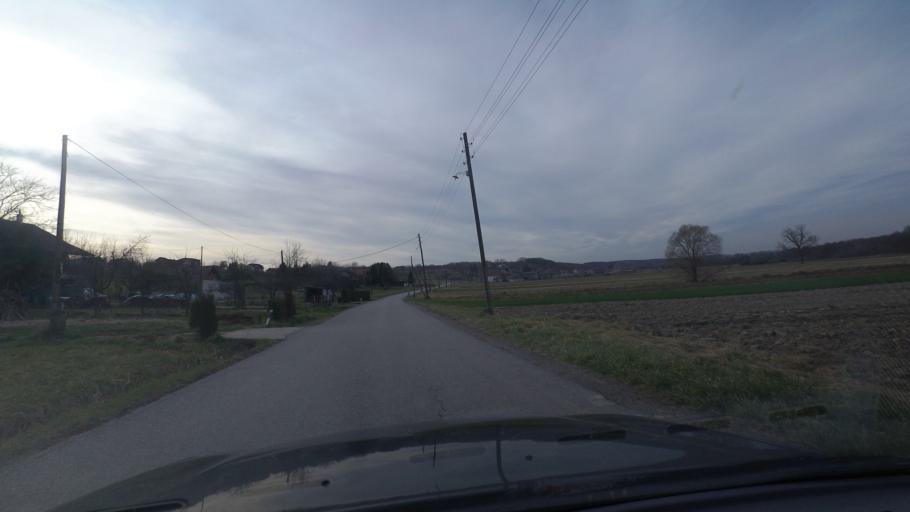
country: HR
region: Grad Zagreb
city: Horvati
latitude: 45.7185
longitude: 15.8181
